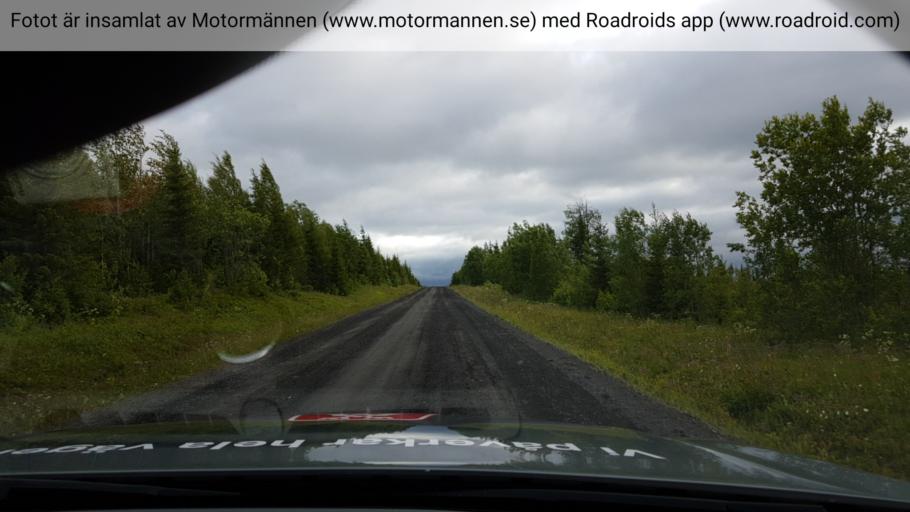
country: SE
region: Jaemtland
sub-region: OEstersunds Kommun
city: Lit
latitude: 63.6294
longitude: 15.0332
